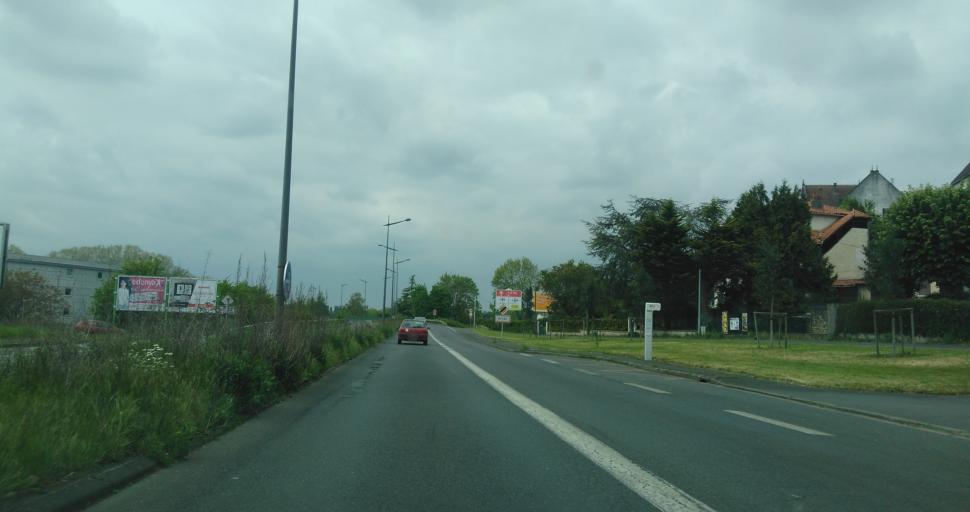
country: FR
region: Poitou-Charentes
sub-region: Departement des Deux-Sevres
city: Niort
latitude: 46.3344
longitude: -0.4752
